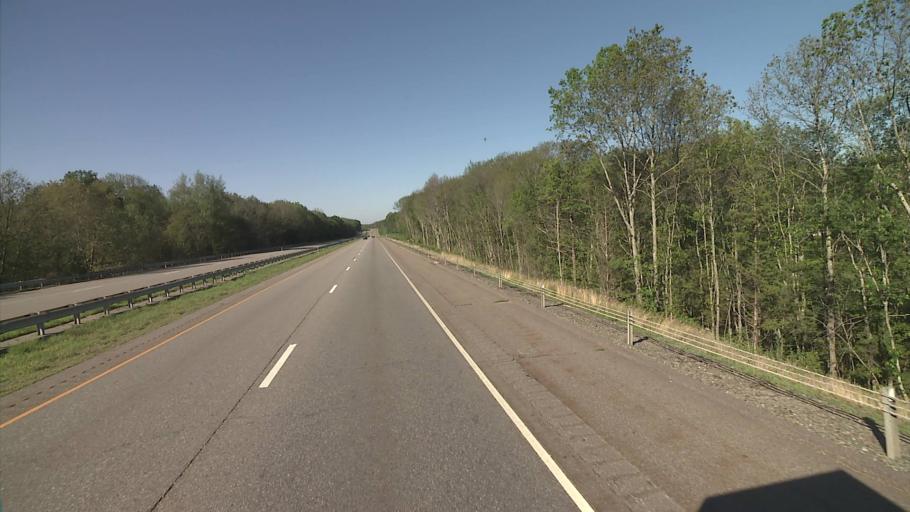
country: US
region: Connecticut
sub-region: Windham County
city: Plainfield Village
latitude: 41.6553
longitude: -71.9252
